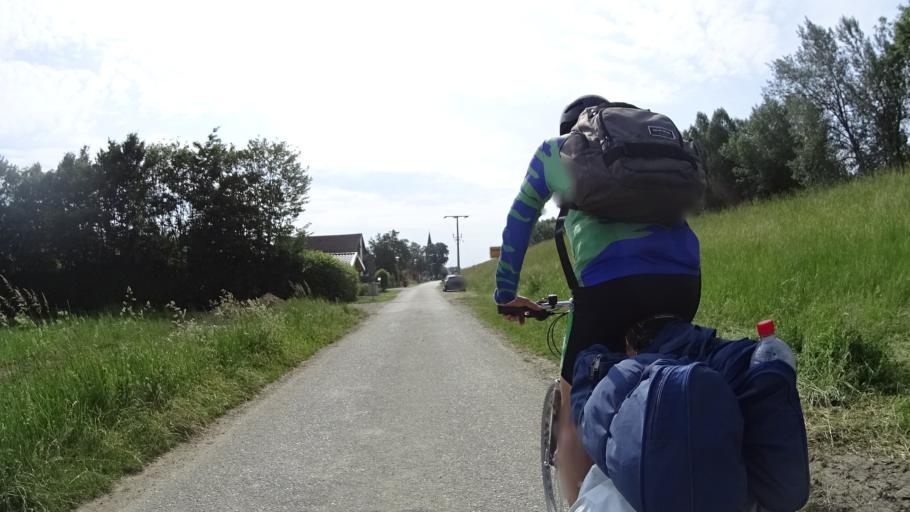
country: DE
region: Bavaria
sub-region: Lower Bavaria
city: Mariaposching
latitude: 48.8278
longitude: 12.7993
